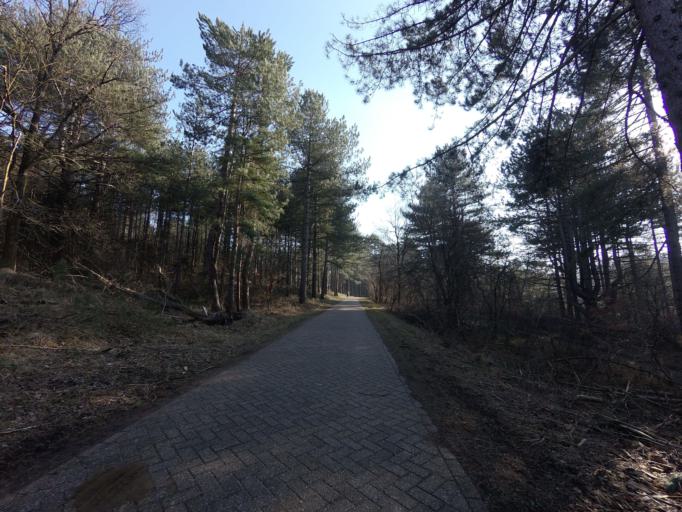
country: NL
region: North Holland
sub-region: Gemeente Bloemendaal
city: Bloemendaal
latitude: 52.4131
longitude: 4.6050
